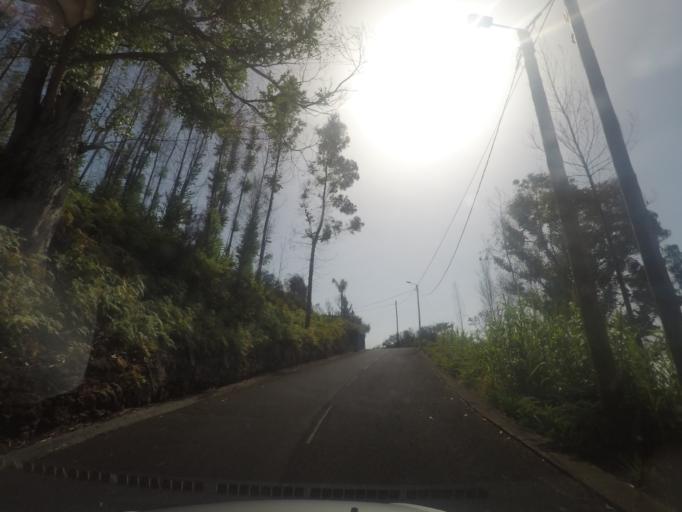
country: PT
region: Madeira
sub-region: Calheta
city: Faja da Ovelha
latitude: 32.8288
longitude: -17.2309
